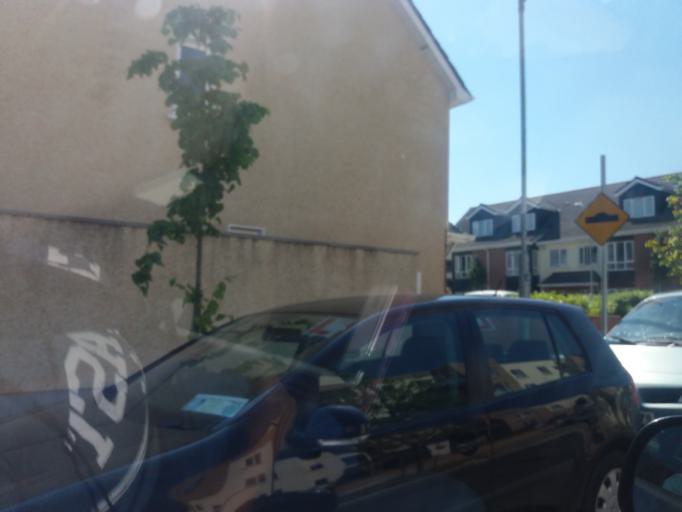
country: IE
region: Leinster
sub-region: Fingal County
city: Swords
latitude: 53.4489
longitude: -6.2426
